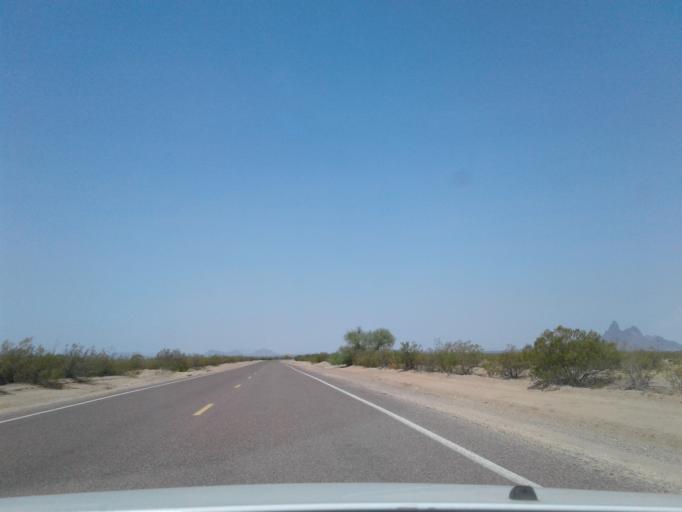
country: US
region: Arizona
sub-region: Pima County
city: Avra Valley
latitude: 32.6121
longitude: -111.2821
